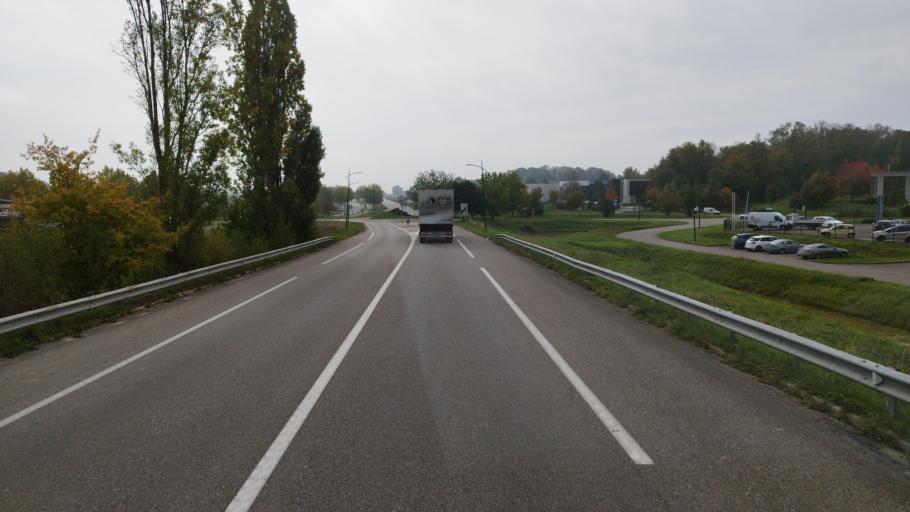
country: FR
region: Alsace
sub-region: Departement du Bas-Rhin
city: Wissembourg
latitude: 49.0230
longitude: 7.9645
